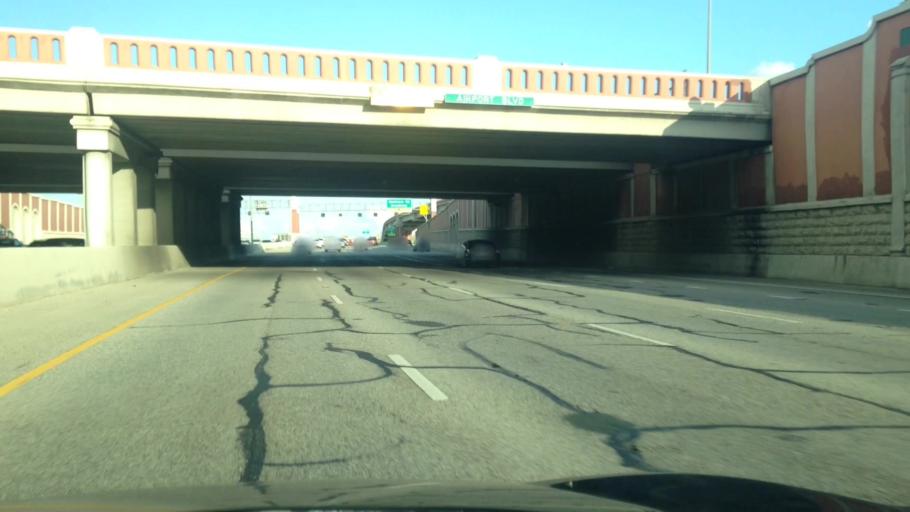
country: US
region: Texas
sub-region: Bexar County
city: Alamo Heights
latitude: 29.5200
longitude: -98.4775
